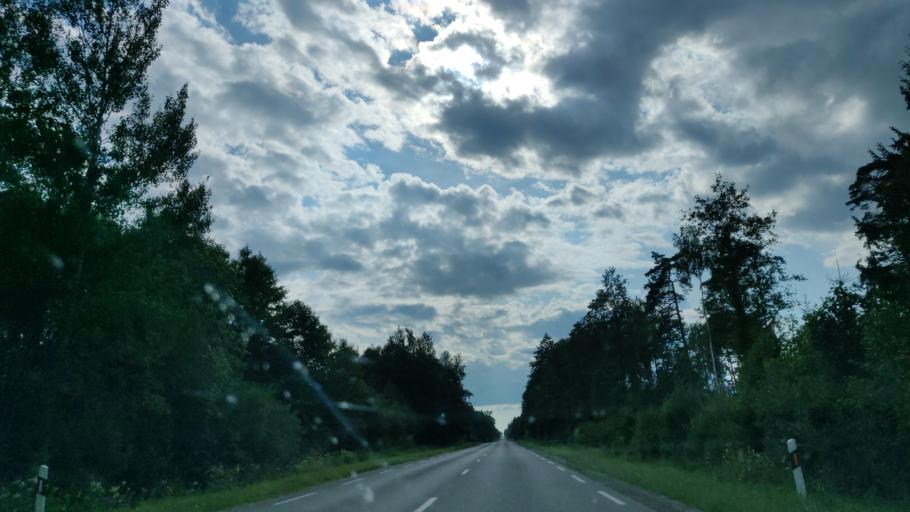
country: LT
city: Rietavas
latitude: 55.7019
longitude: 21.7854
